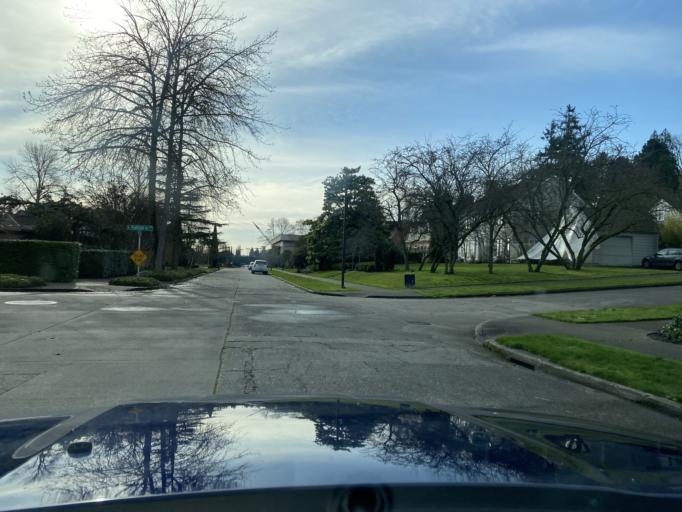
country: US
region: Washington
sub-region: King County
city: Medina
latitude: 47.6299
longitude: -122.2800
